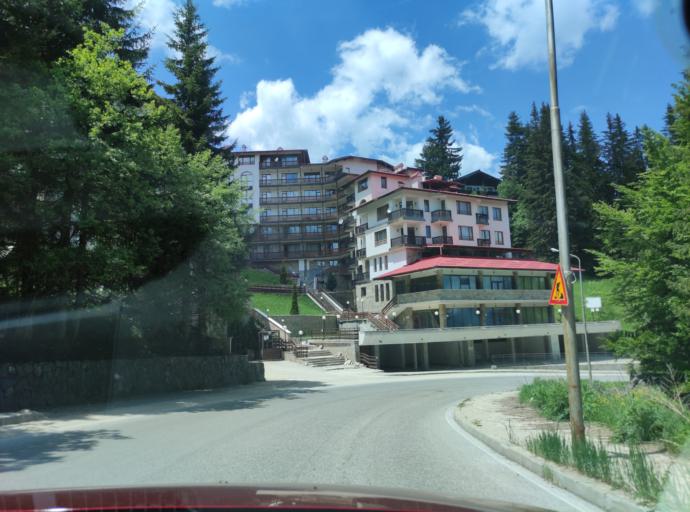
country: BG
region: Smolyan
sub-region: Obshtina Smolyan
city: Smolyan
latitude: 41.6472
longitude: 24.6982
